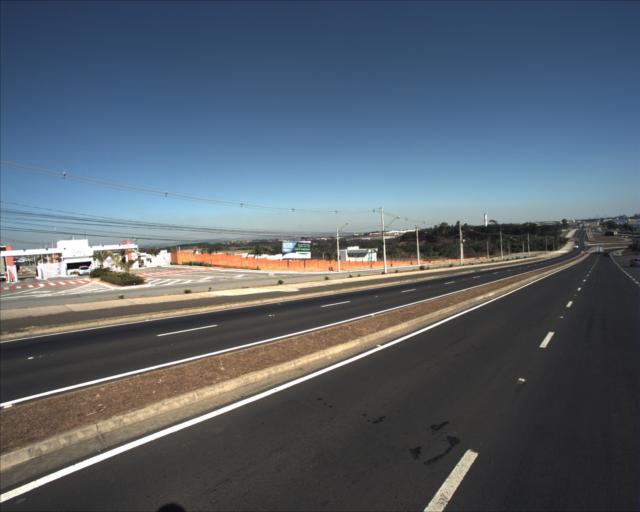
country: BR
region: Sao Paulo
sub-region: Sorocaba
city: Sorocaba
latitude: -23.4084
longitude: -47.3846
